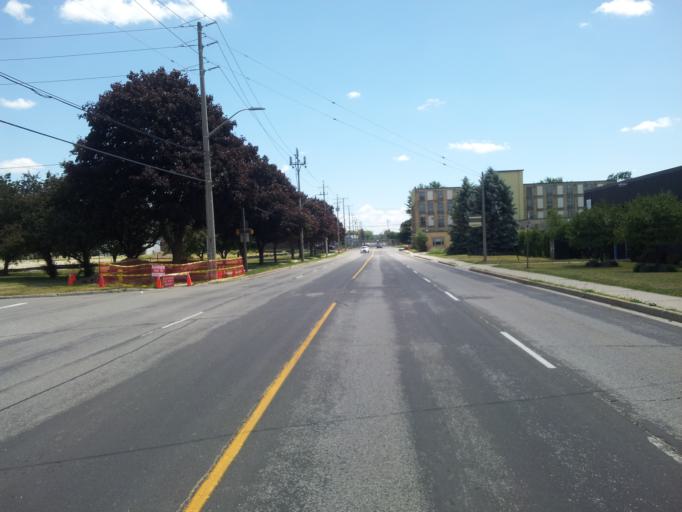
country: CA
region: Ontario
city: Stratford
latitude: 43.3689
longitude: -80.9632
